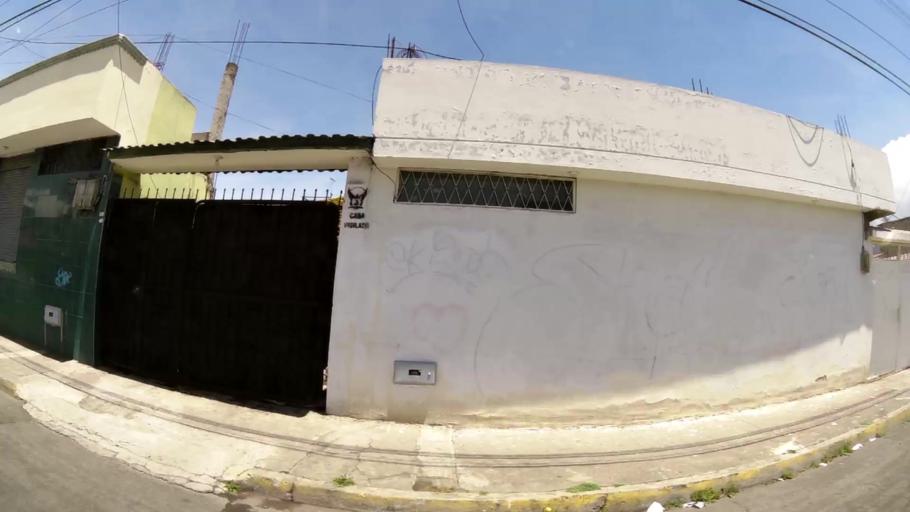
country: EC
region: Chimborazo
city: Riobamba
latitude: -1.6741
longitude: -78.6370
